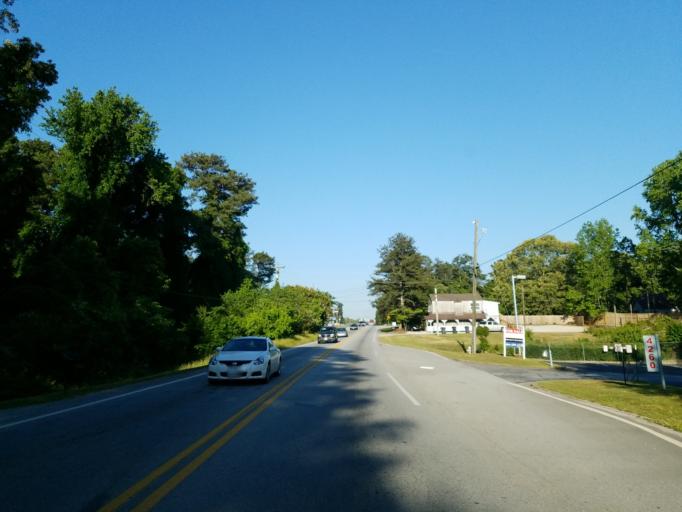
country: US
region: Georgia
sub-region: Douglas County
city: Lithia Springs
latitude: 33.7934
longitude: -84.6790
